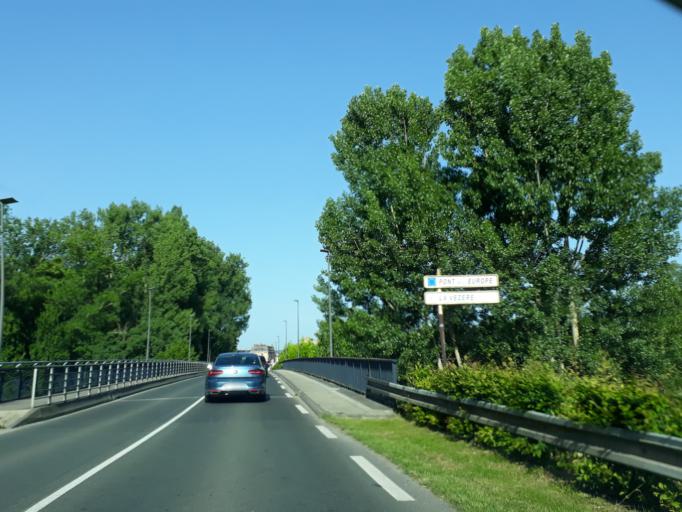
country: FR
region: Aquitaine
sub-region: Departement de la Dordogne
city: Terrasson-Lavilledieu
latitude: 45.1300
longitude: 1.3085
